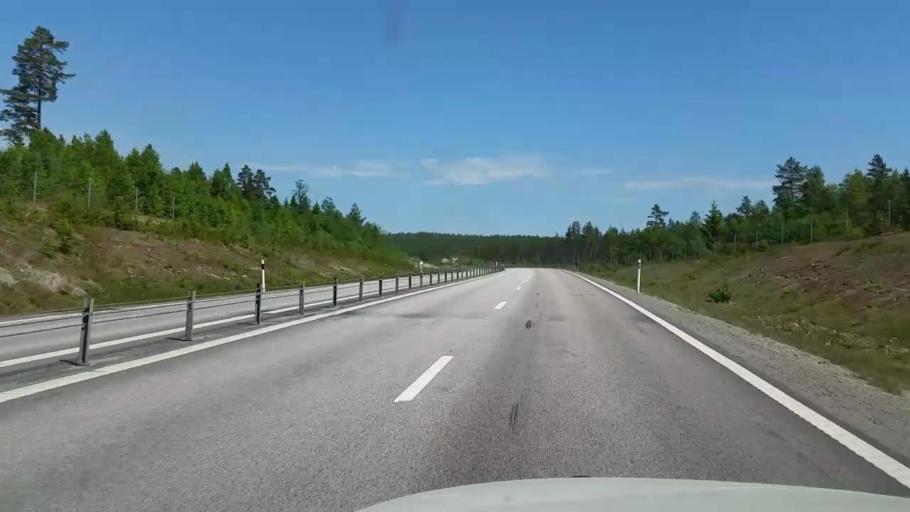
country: SE
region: Gaevleborg
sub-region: Hudiksvalls Kommun
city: Hudiksvall
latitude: 61.7211
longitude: 17.0585
